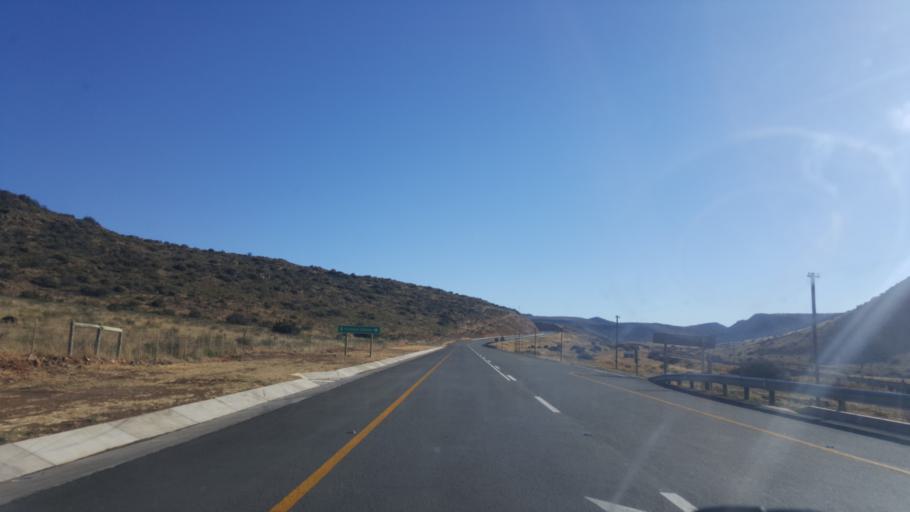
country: ZA
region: Eastern Cape
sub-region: Chris Hani District Municipality
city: Middelburg
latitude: -31.3856
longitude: 25.0316
